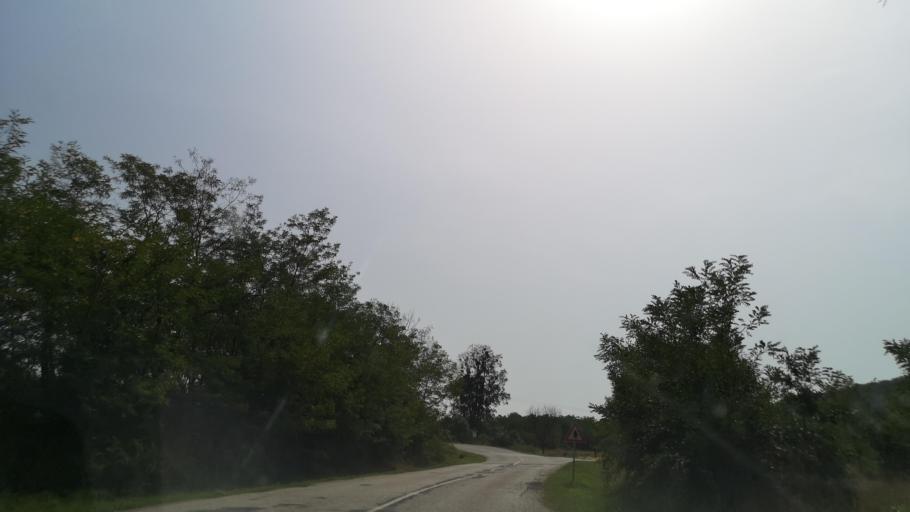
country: SK
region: Banskobystricky
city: Revuca
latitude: 48.5989
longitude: 20.1433
